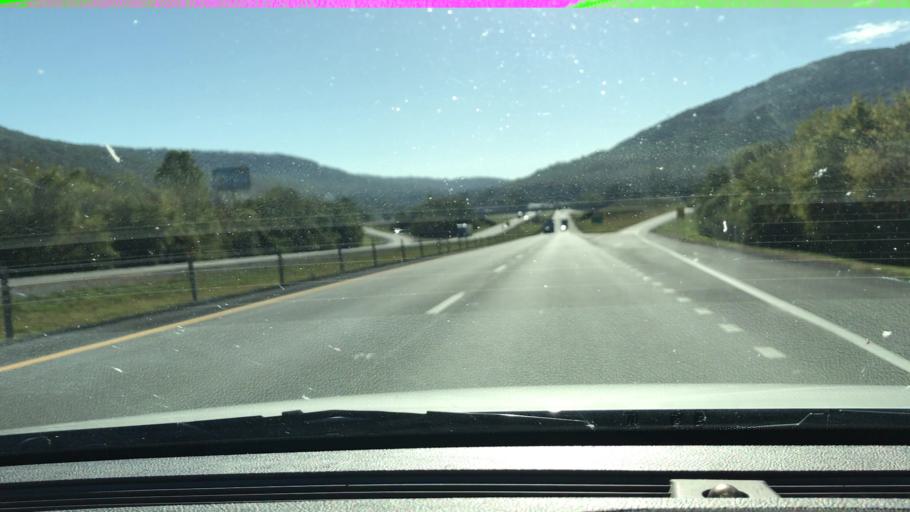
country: US
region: Tennessee
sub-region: Cumberland County
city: Fairfield Glade
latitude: 35.9073
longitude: -84.8818
